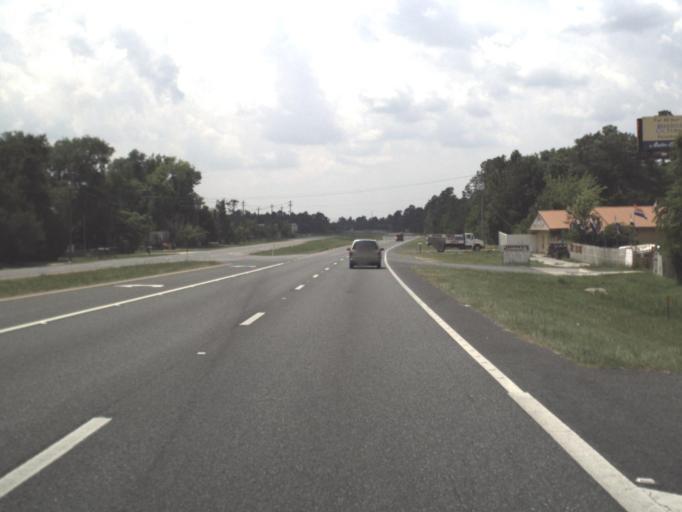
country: US
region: Florida
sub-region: Putnam County
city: Palatka
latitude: 29.6943
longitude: -81.6633
